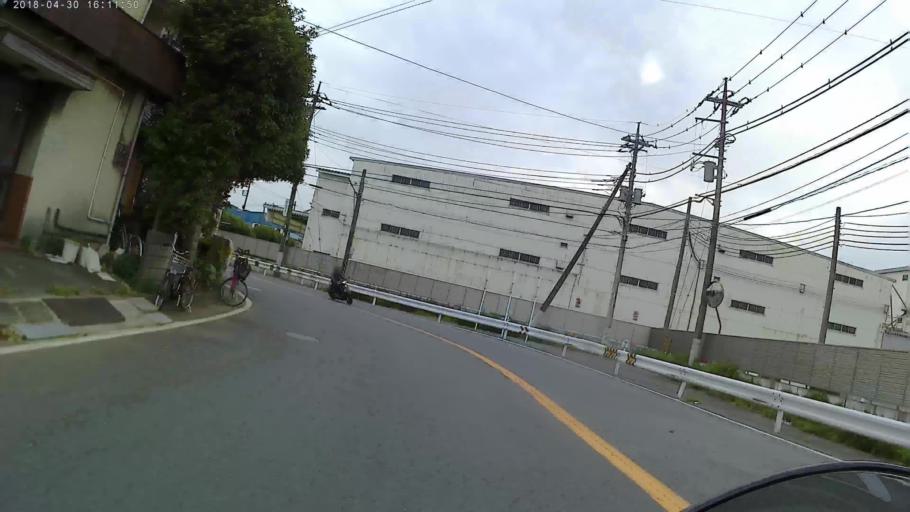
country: JP
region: Kanagawa
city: Minami-rinkan
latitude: 35.4999
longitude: 139.4281
